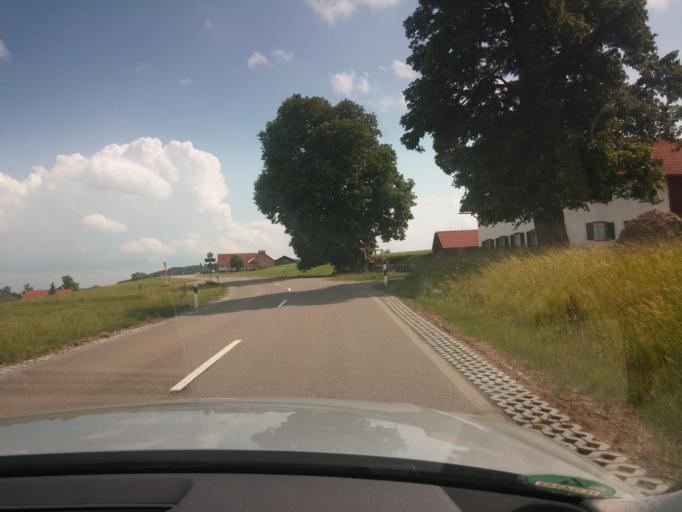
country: DE
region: Bavaria
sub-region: Swabia
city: Altusried
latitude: 47.7885
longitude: 10.2108
